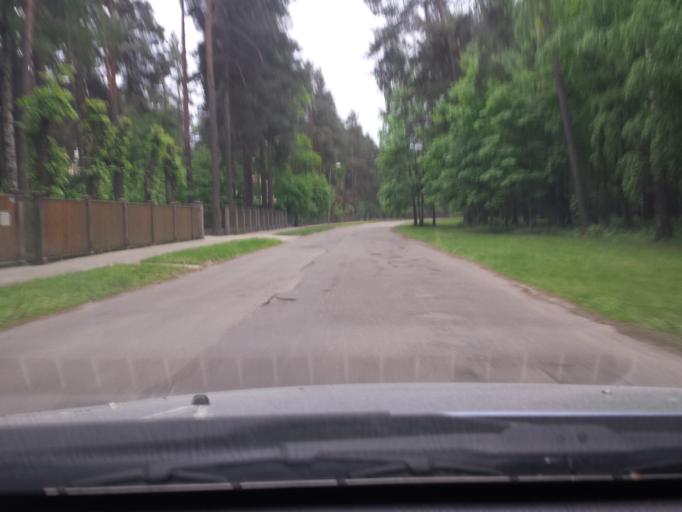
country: LV
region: Riga
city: Jaunciems
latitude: 56.9999
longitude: 24.1524
